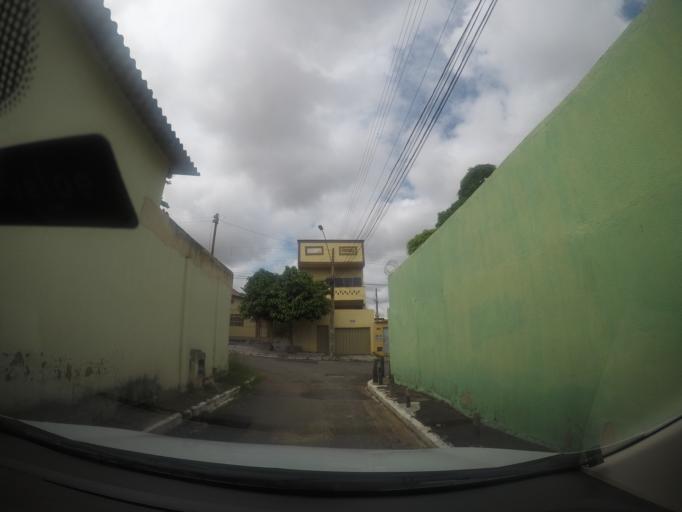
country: BR
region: Goias
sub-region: Goiania
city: Goiania
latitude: -16.6659
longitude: -49.2966
